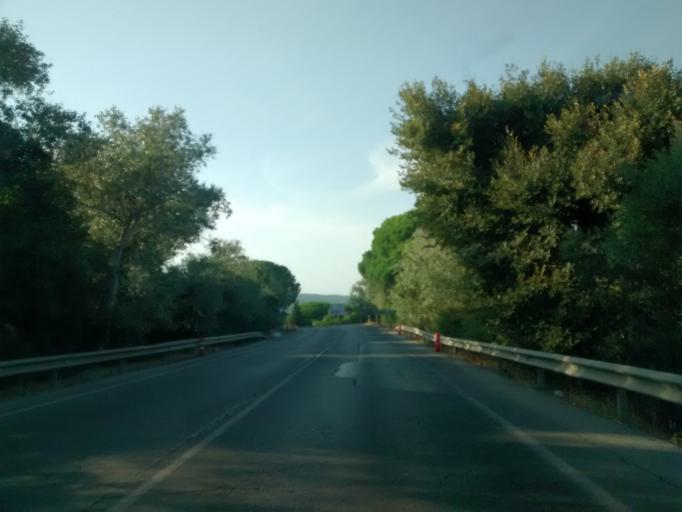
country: ES
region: Andalusia
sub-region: Provincia de Cadiz
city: Barbate de Franco
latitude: 36.2133
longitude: -5.9404
